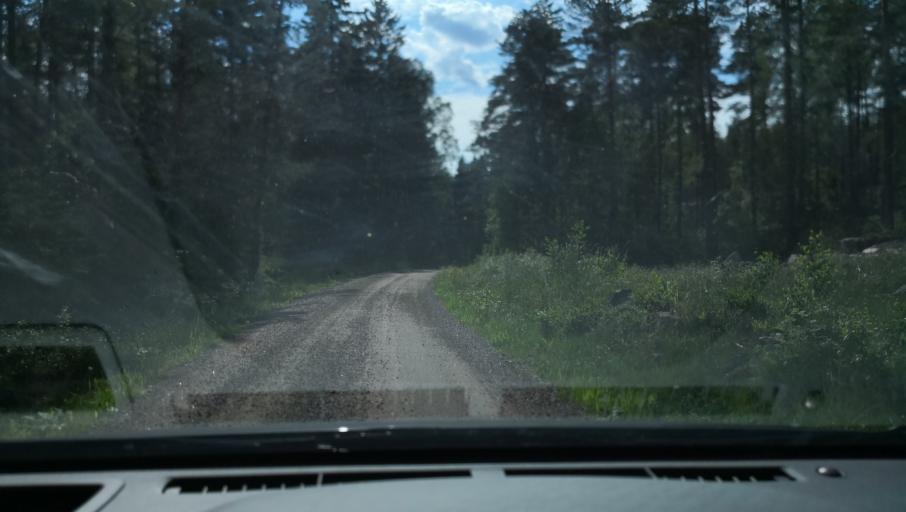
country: SE
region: Uppsala
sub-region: Enkopings Kommun
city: Orsundsbro
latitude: 59.8385
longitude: 17.2667
